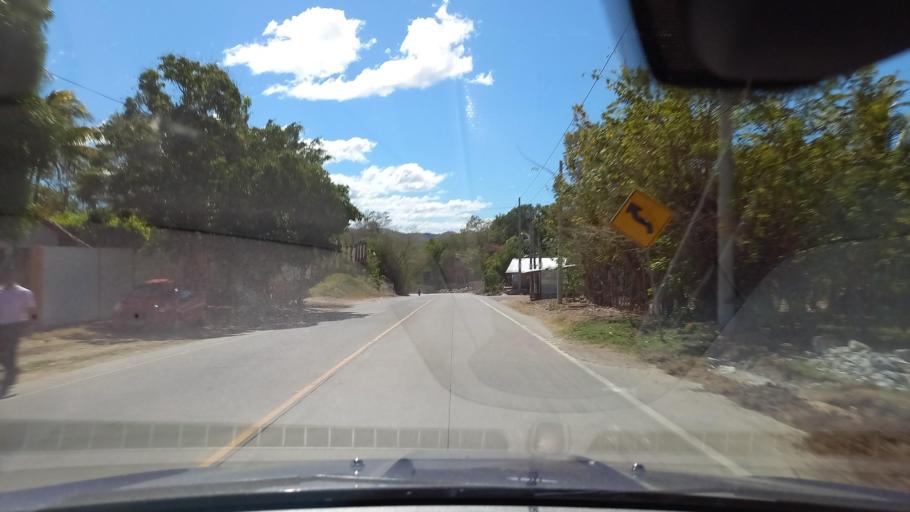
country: SV
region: Santa Ana
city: Metapan
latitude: 14.3539
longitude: -89.4541
